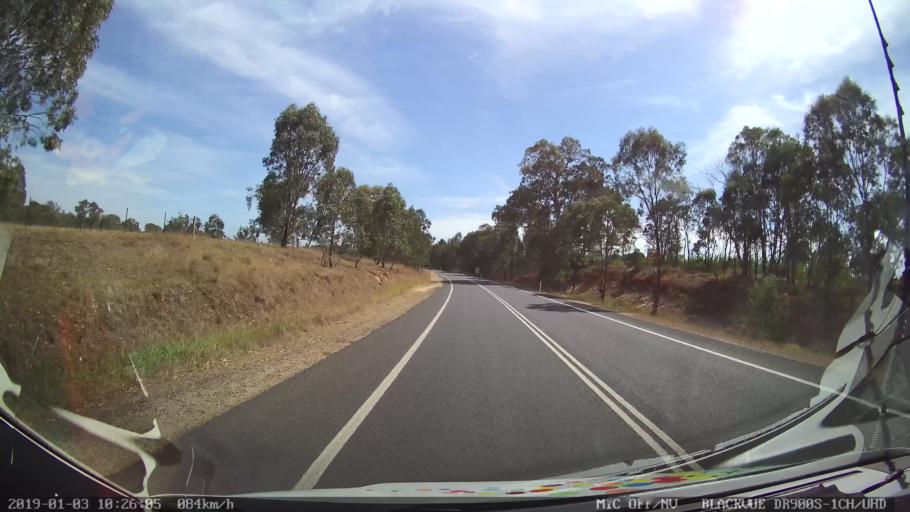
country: AU
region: New South Wales
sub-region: Young
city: Young
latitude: -34.4168
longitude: 148.2471
